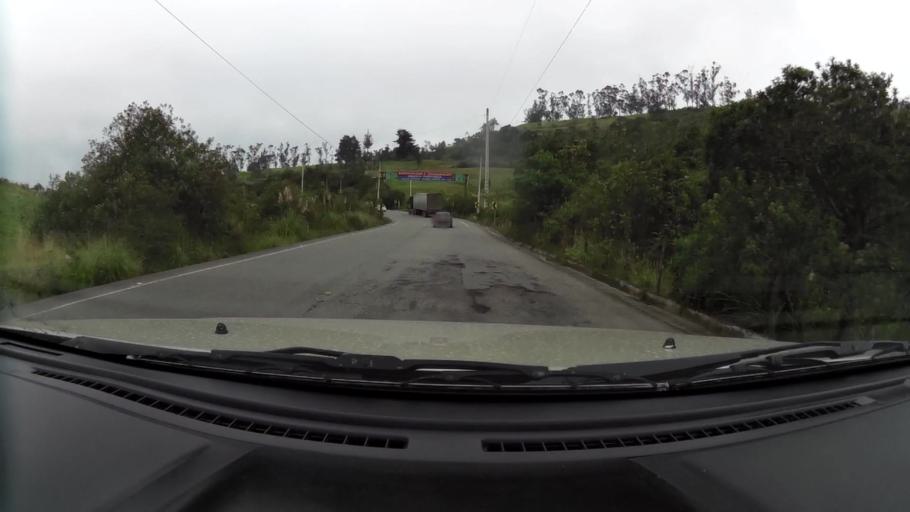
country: EC
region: Canar
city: Canar
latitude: -2.3932
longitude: -78.9680
